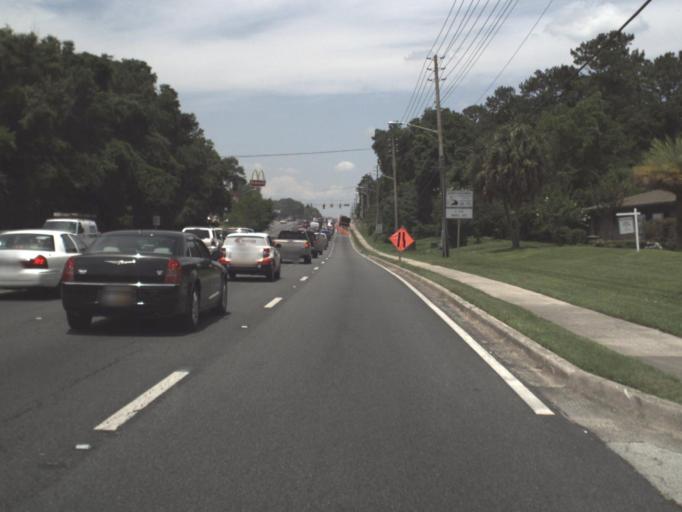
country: US
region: Florida
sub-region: Alachua County
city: Gainesville
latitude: 29.6597
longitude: -82.4037
